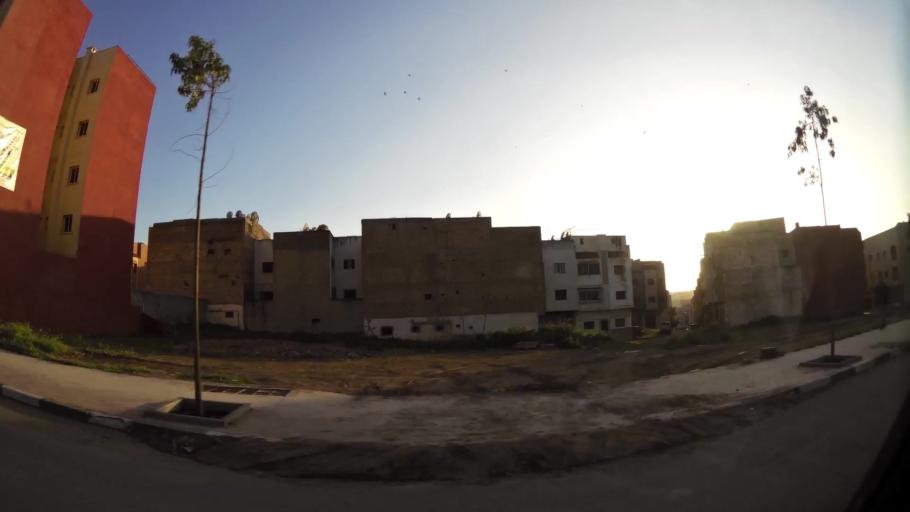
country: MA
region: Chaouia-Ouardigha
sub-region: Settat Province
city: Settat
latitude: 32.9937
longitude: -7.6146
